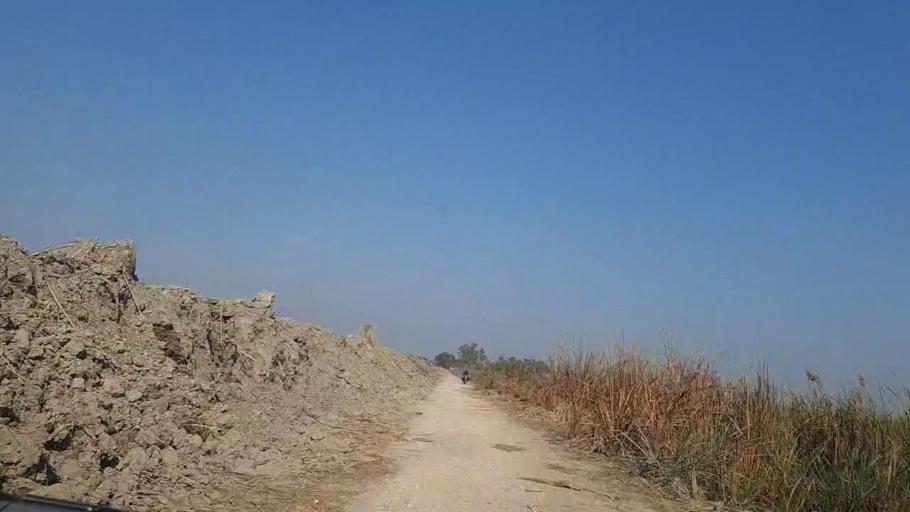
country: PK
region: Sindh
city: Sakrand
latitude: 26.0893
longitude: 68.3680
